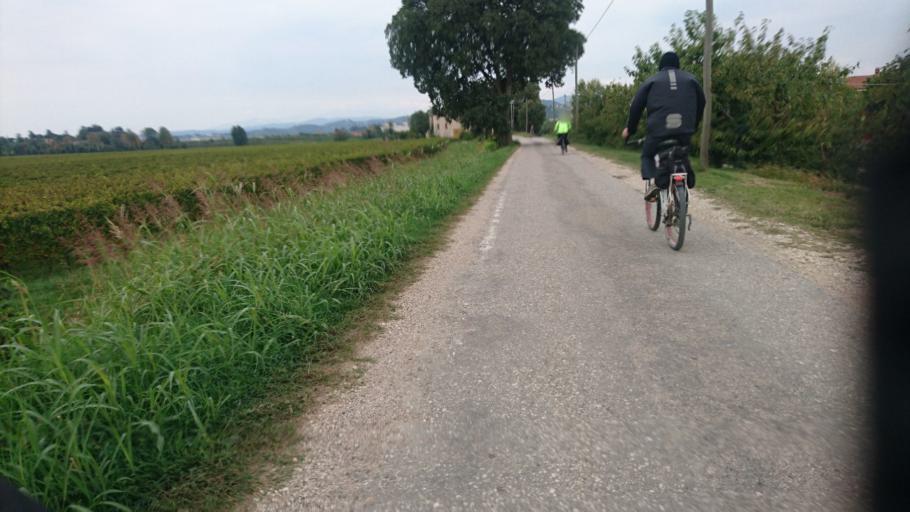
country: IT
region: Veneto
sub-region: Provincia di Verona
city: Caldierino-Rota
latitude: 45.4032
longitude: 11.1427
